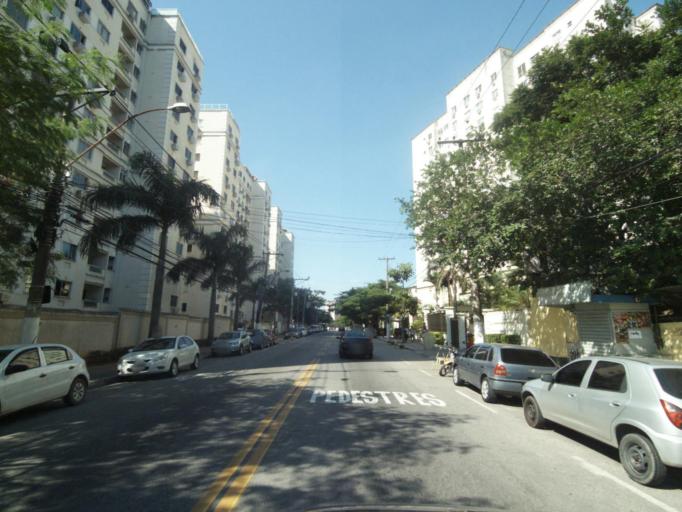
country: BR
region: Rio de Janeiro
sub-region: Niteroi
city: Niteroi
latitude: -22.8636
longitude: -43.0976
